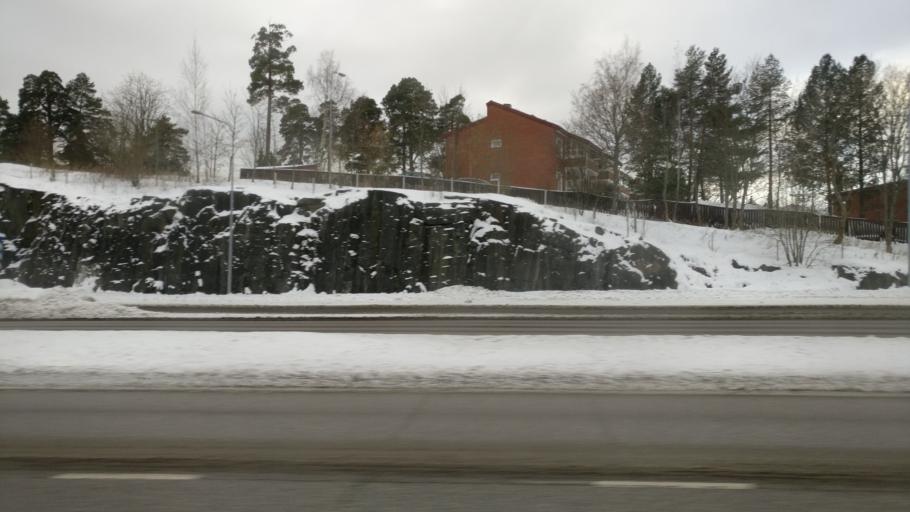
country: FI
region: Uusimaa
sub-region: Helsinki
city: Vantaa
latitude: 60.1856
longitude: 25.0457
